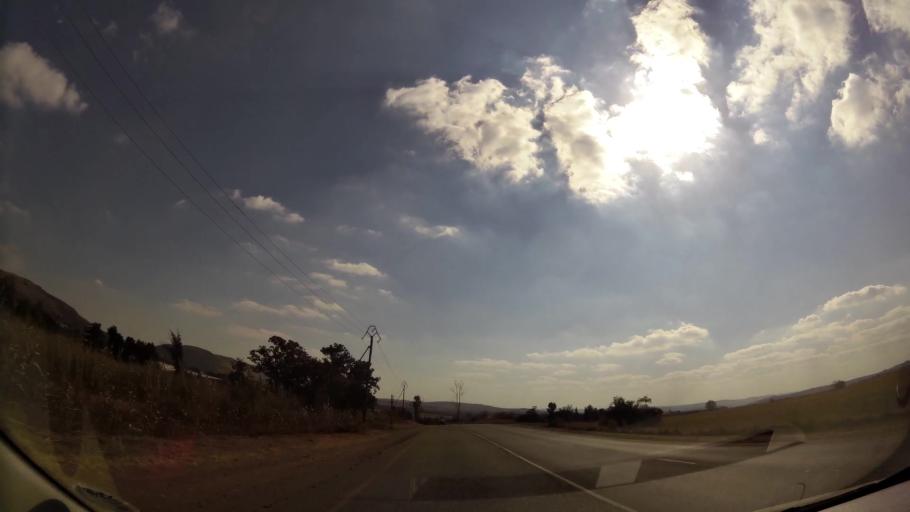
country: ZA
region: Gauteng
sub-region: West Rand District Municipality
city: Muldersdriseloop
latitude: -26.0421
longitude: 27.7919
